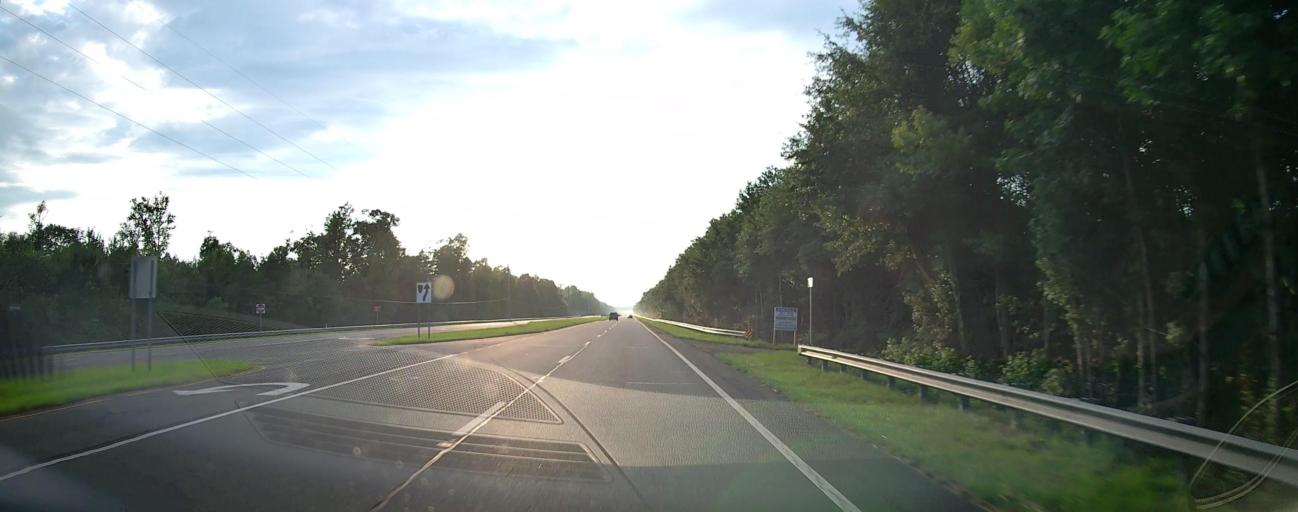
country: US
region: Georgia
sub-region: Taylor County
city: Reynolds
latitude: 32.5449
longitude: -84.0350
